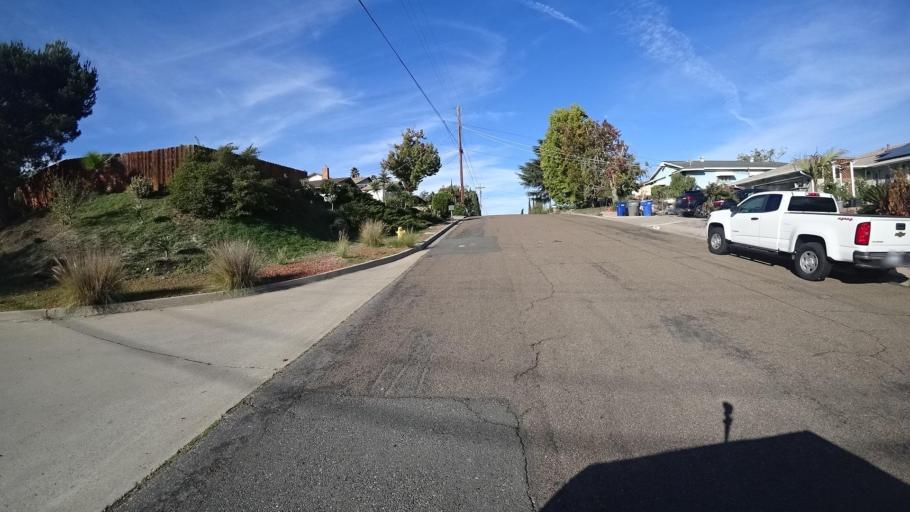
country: US
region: California
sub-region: San Diego County
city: Spring Valley
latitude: 32.7392
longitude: -116.9759
